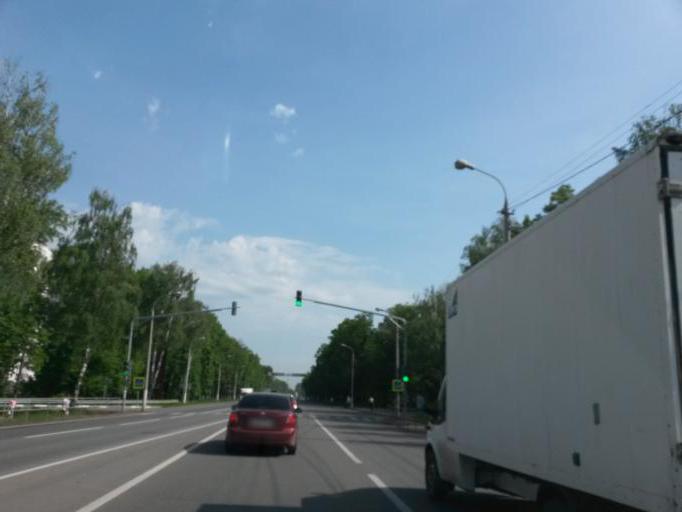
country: RU
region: Moskovskaya
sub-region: Chekhovskiy Rayon
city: Chekhov
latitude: 55.1657
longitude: 37.4679
